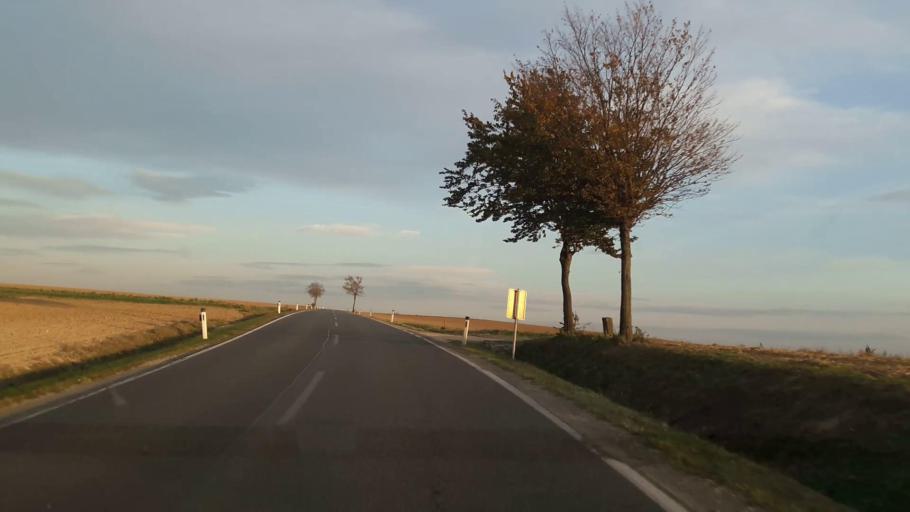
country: AT
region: Lower Austria
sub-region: Politischer Bezirk Korneuburg
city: Grossrussbach
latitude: 48.4533
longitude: 16.3745
